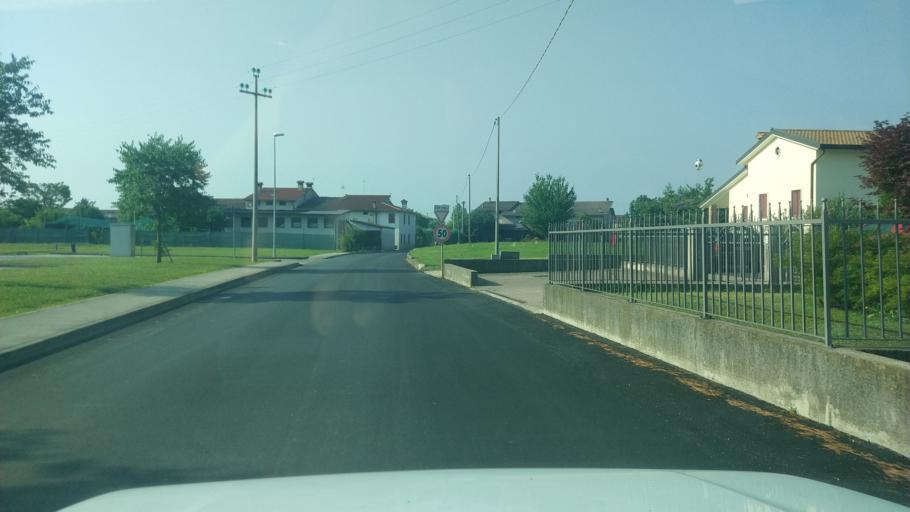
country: IT
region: Veneto
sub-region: Provincia di Vicenza
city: Mason Vicentino
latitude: 45.7173
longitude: 11.6301
